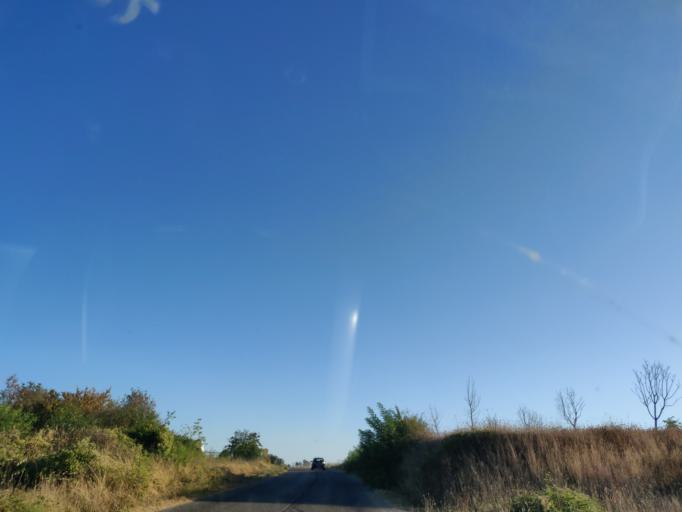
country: IT
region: Latium
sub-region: Provincia di Viterbo
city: Grotte di Castro
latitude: 42.6951
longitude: 11.8781
